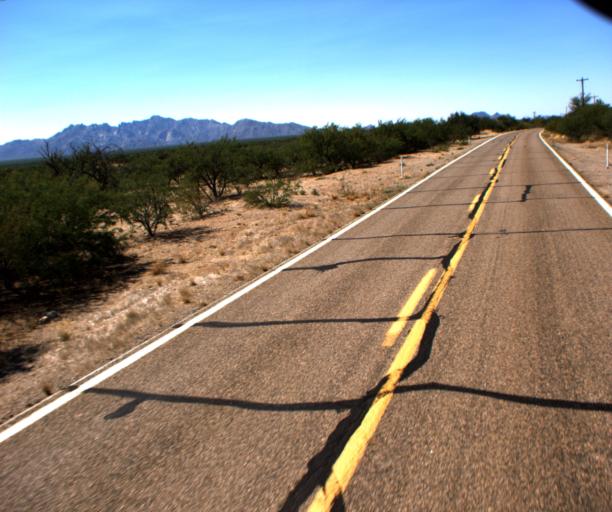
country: US
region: Arizona
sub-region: Pima County
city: Three Points
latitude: 31.8791
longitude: -111.3958
